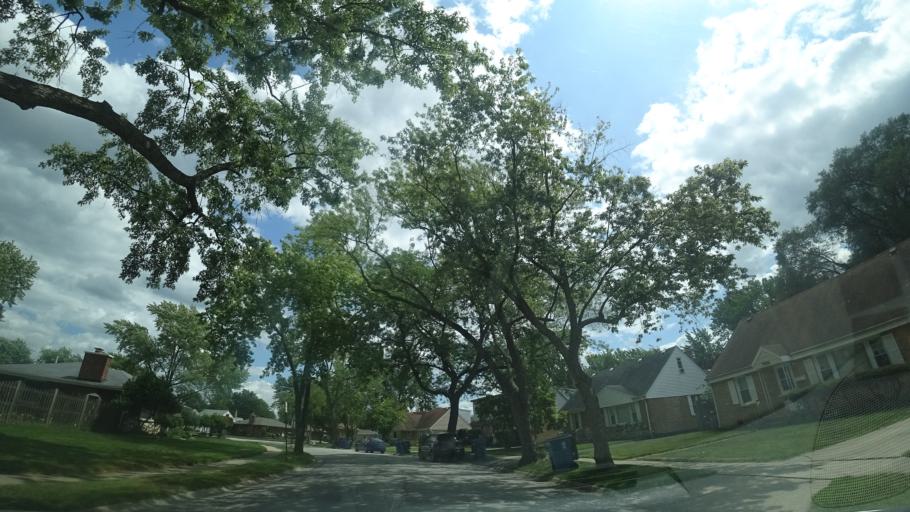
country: US
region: Illinois
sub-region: Cook County
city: Alsip
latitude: 41.6809
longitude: -87.7358
